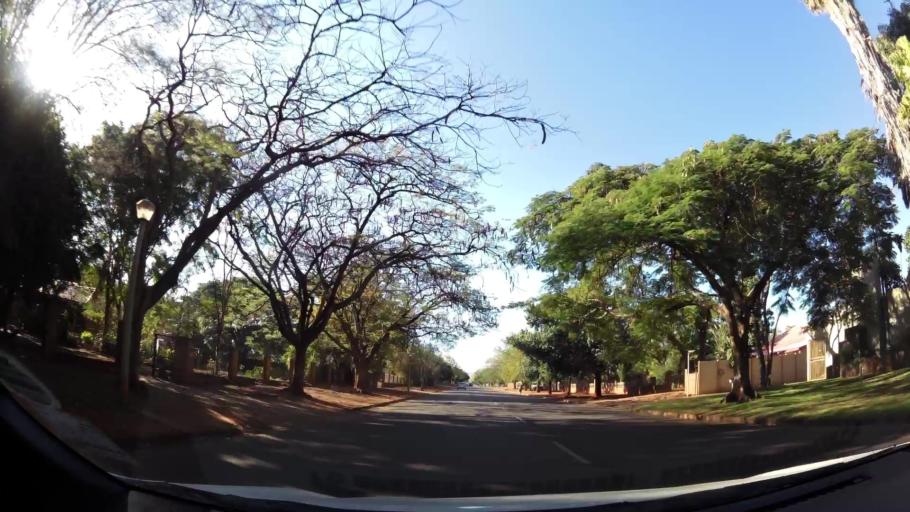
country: ZA
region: Limpopo
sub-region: Waterberg District Municipality
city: Mokopane
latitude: -24.1934
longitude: 29.0115
